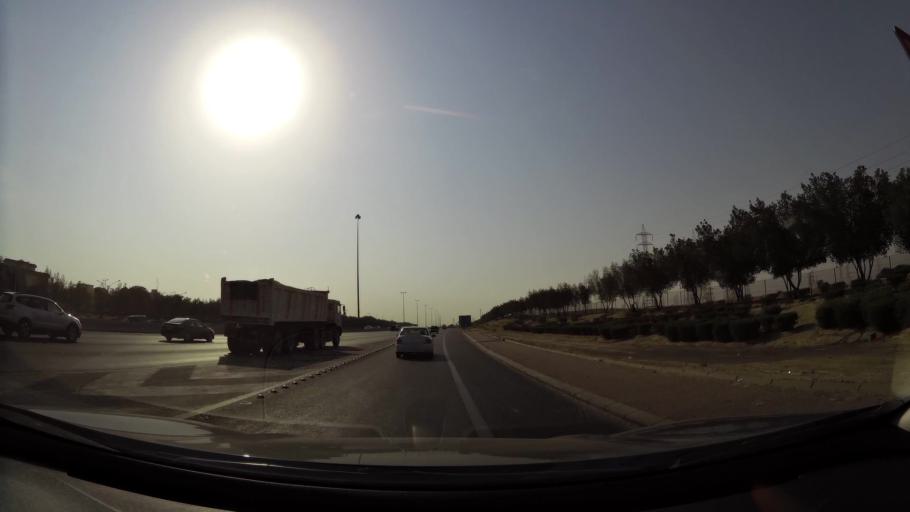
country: KW
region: Al Ahmadi
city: Ar Riqqah
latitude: 29.1518
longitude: 48.0801
